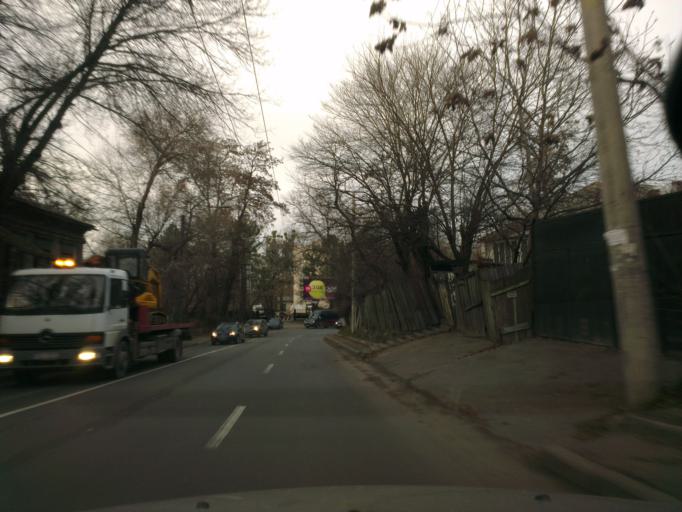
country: MD
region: Chisinau
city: Chisinau
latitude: 47.0318
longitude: 28.8167
